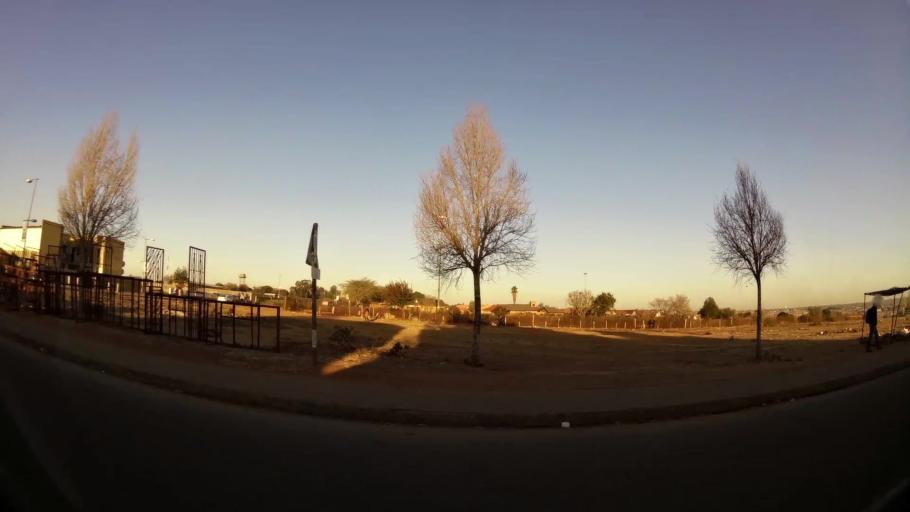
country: ZA
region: Gauteng
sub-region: Ekurhuleni Metropolitan Municipality
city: Tembisa
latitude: -26.0075
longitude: 28.2142
